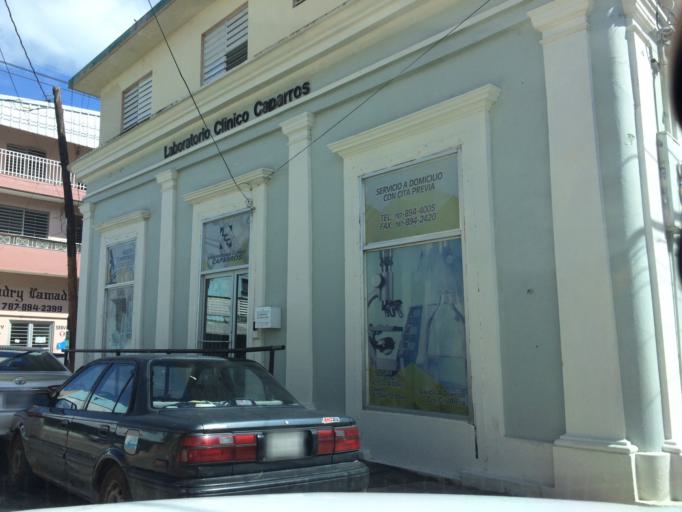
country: PR
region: Utuado
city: Utuado
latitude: 18.2656
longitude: -66.7009
